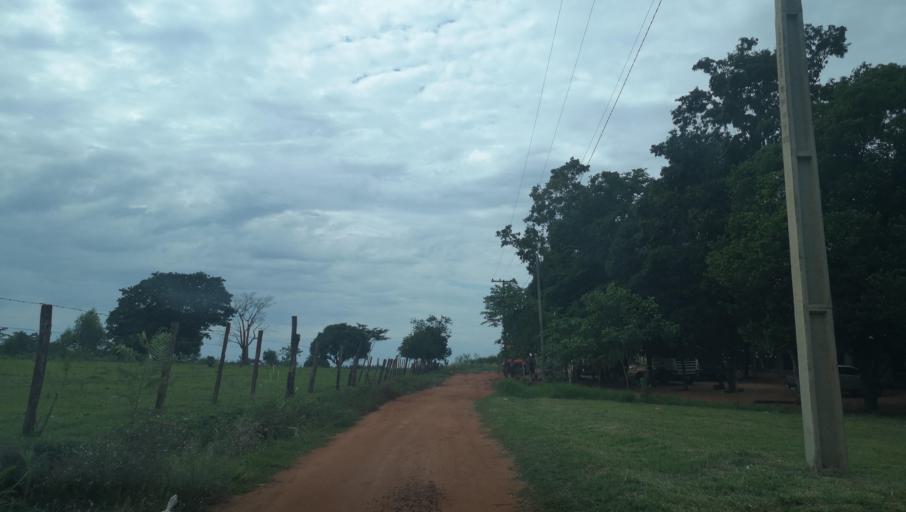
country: PY
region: San Pedro
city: Capiibary
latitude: -24.7146
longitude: -56.0116
